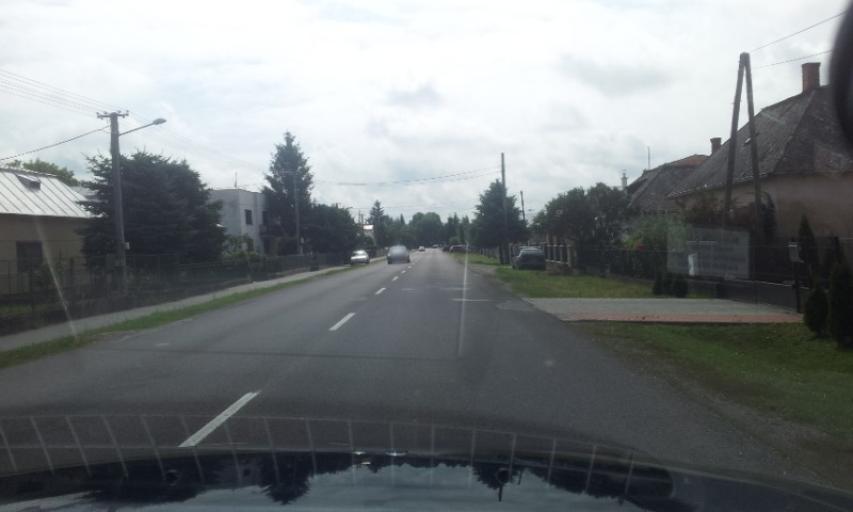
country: SK
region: Kosicky
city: Michalovce
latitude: 48.7380
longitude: 21.9482
